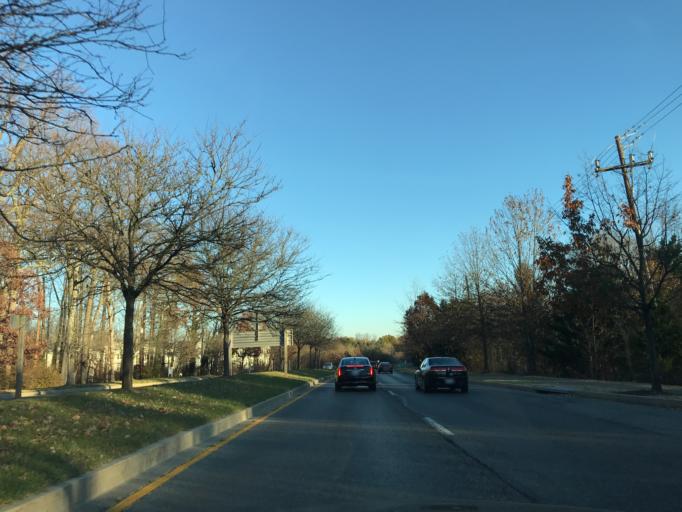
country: US
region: Maryland
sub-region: Montgomery County
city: Olney
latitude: 39.1493
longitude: -77.0568
